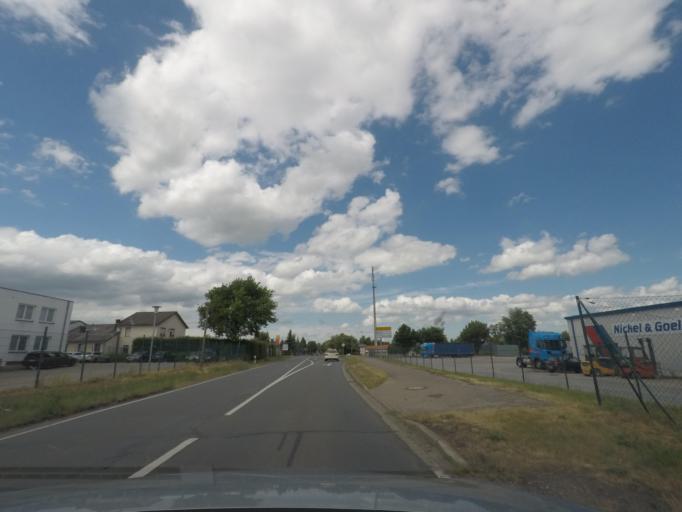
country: DE
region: Saxony-Anhalt
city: Schwanebeck
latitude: 51.9592
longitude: 11.1217
